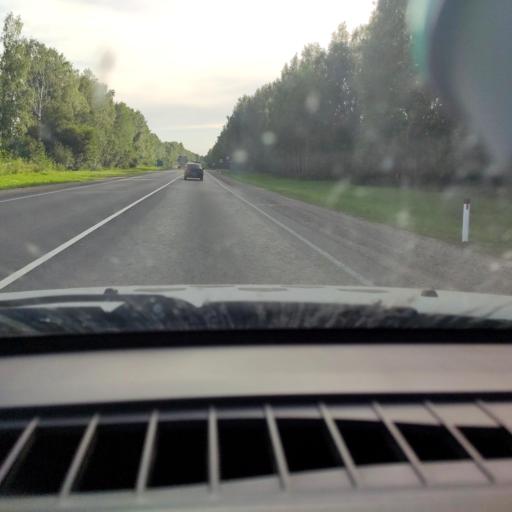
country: RU
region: Kirov
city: Vakhrushi
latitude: 58.6475
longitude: 49.8623
